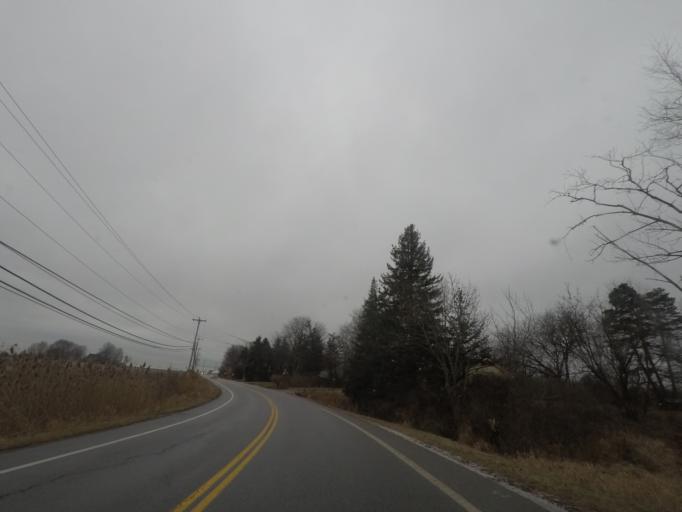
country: US
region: New York
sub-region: Saratoga County
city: Mechanicville
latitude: 42.8933
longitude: -73.7194
